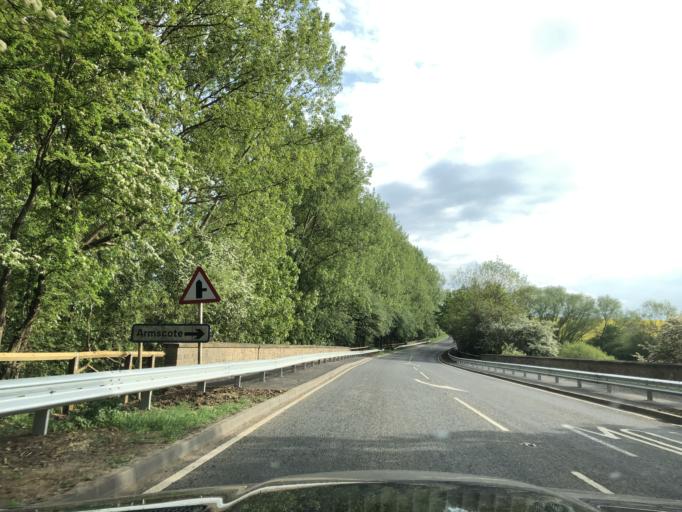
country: GB
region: England
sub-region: Warwickshire
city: Shipston on Stour
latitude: 52.1061
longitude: -1.6224
